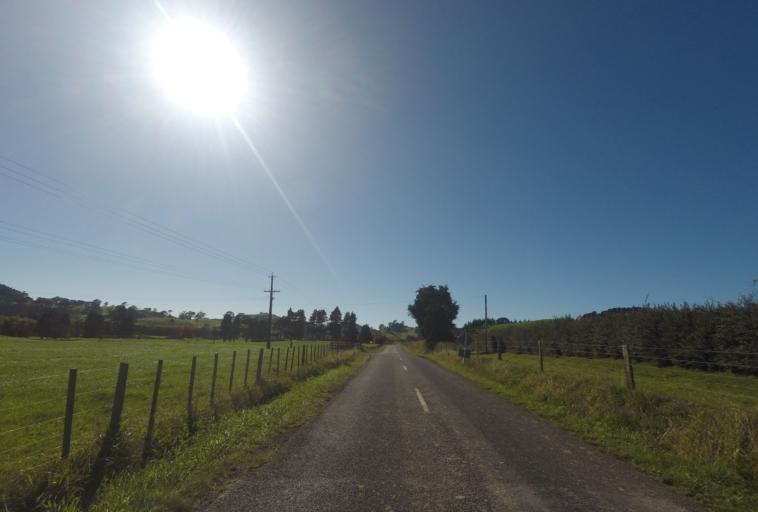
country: NZ
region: Bay of Plenty
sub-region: Western Bay of Plenty District
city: Waihi Beach
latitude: -37.4118
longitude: 175.8919
